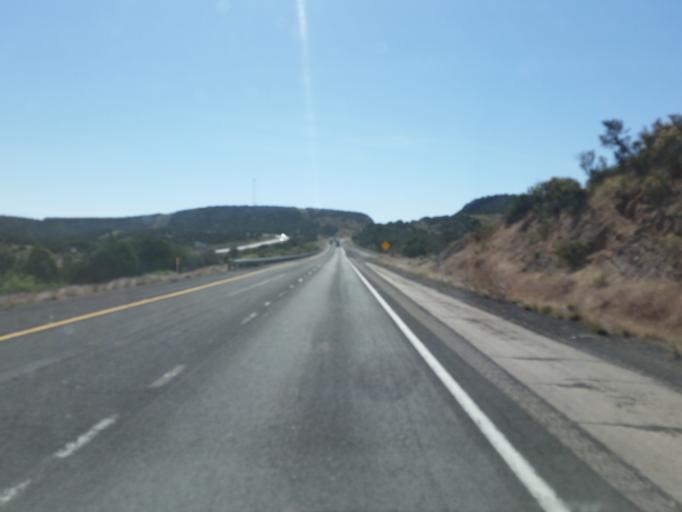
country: US
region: Arizona
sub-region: Mohave County
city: Peach Springs
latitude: 35.1901
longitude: -113.4332
